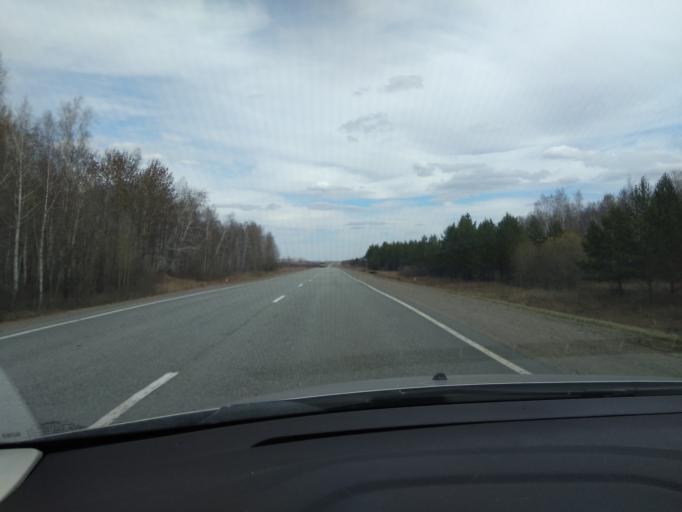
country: RU
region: Sverdlovsk
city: Yelanskiy
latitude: 56.7684
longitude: 62.4326
